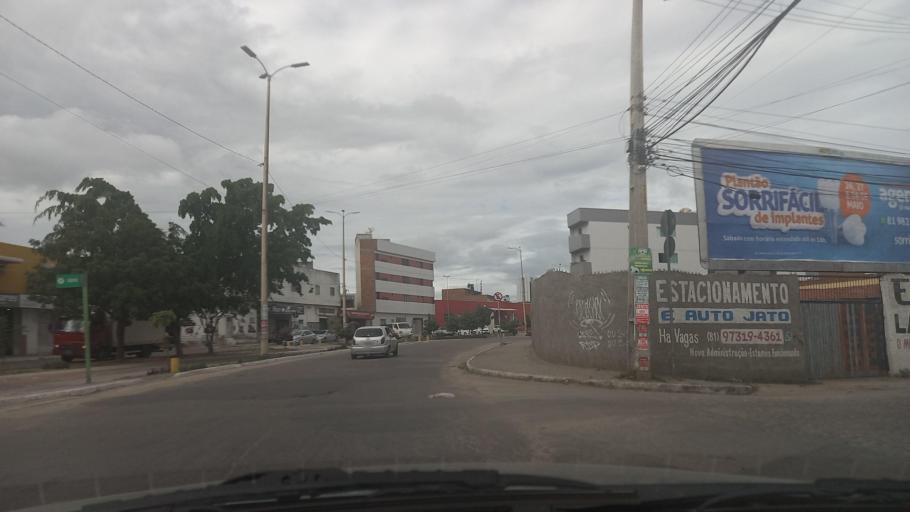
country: BR
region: Pernambuco
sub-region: Caruaru
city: Caruaru
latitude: -8.2758
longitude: -35.9845
